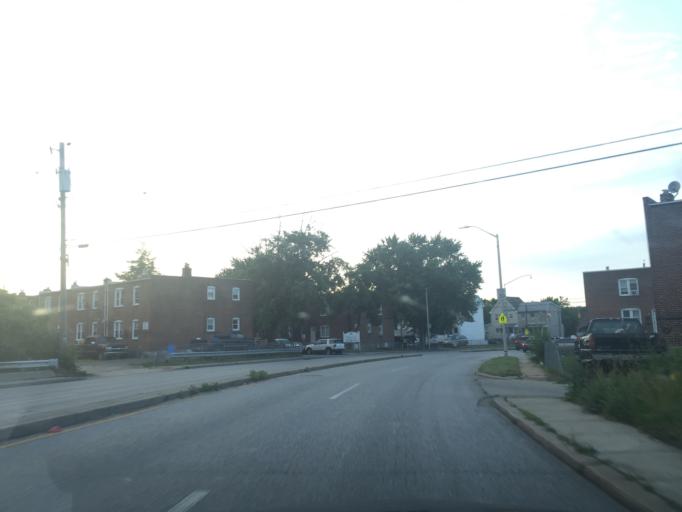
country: US
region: Maryland
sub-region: Anne Arundel County
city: Brooklyn Park
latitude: 39.2354
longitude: -76.6122
